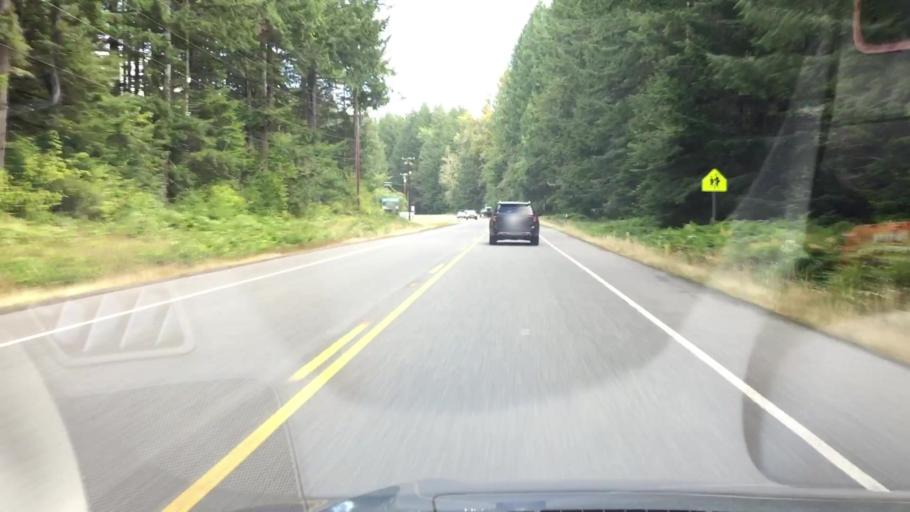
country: US
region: Washington
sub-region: Pierce County
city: Eatonville
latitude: 46.7537
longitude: -122.1127
